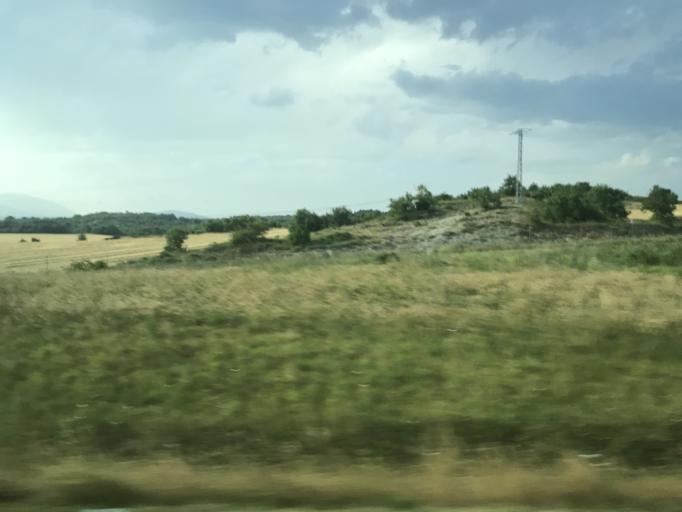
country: ES
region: Basque Country
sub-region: Provincia de Alava
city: Gasteiz / Vitoria
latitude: 42.9179
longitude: -2.6837
